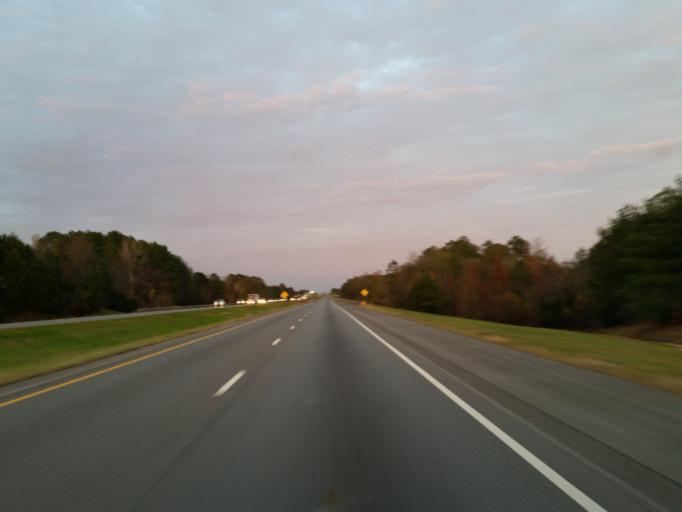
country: US
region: Alabama
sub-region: Sumter County
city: Livingston
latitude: 32.7286
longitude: -88.1098
